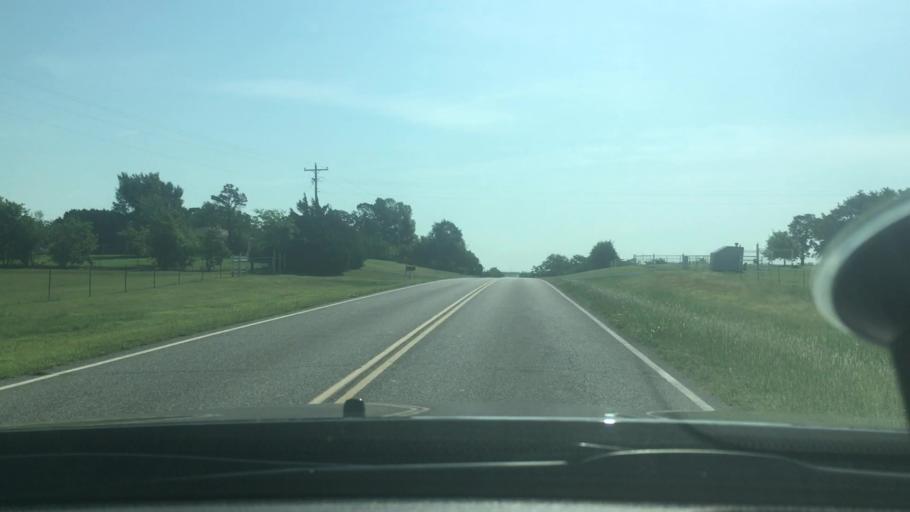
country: US
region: Oklahoma
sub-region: Garvin County
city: Pauls Valley
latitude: 34.6520
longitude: -97.3438
